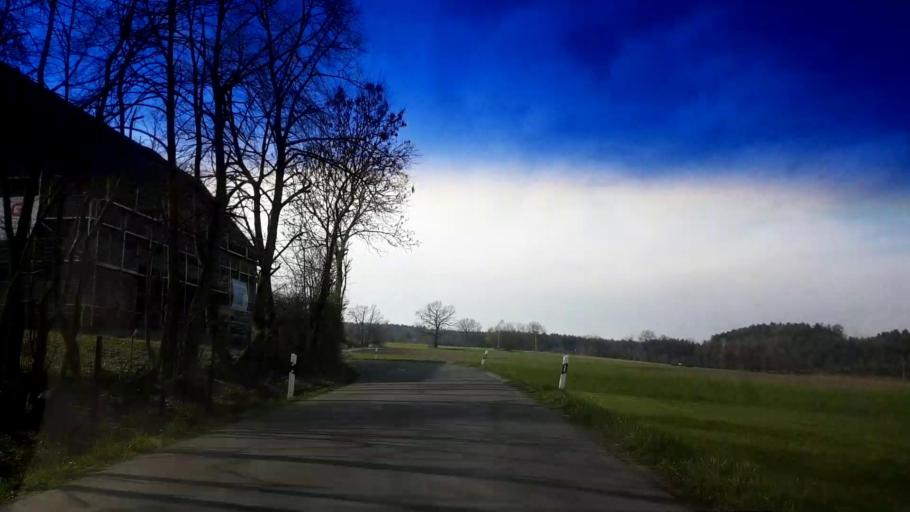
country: DE
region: Bavaria
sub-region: Upper Franconia
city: Himmelkron
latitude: 50.0295
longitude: 11.6222
